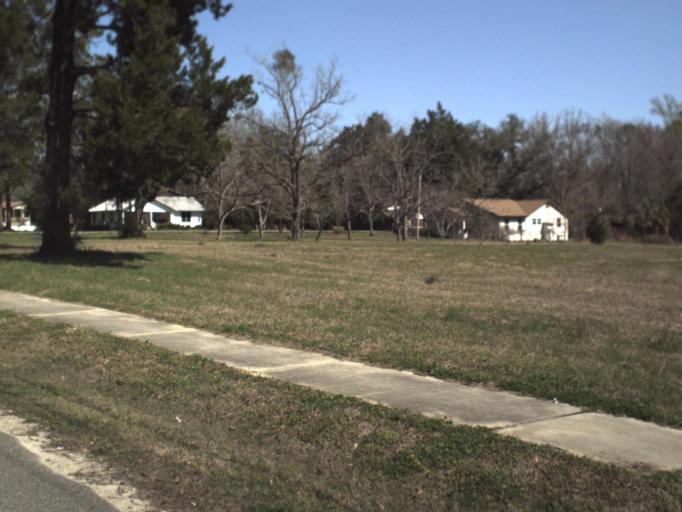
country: US
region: Florida
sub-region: Calhoun County
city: Blountstown
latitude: 30.4521
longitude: -85.0450
